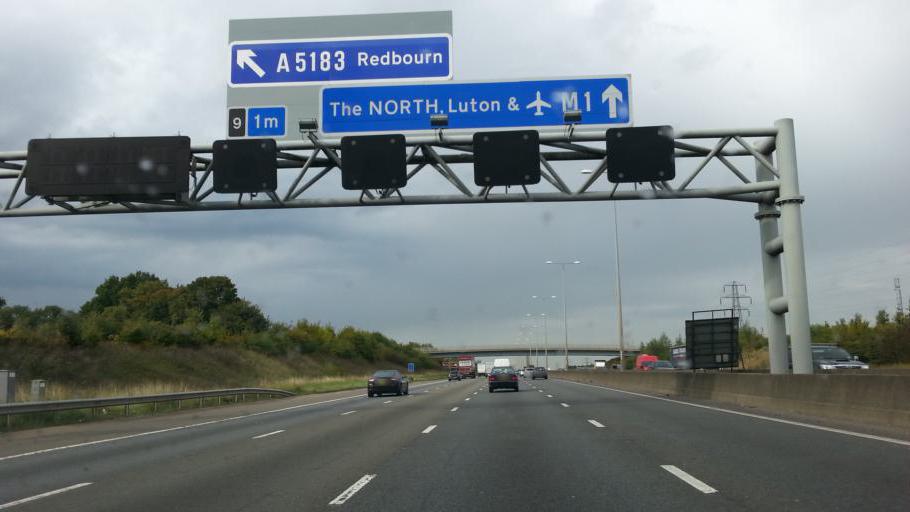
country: GB
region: England
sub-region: Hertfordshire
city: Redbourn
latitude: 51.8004
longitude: -0.4134
